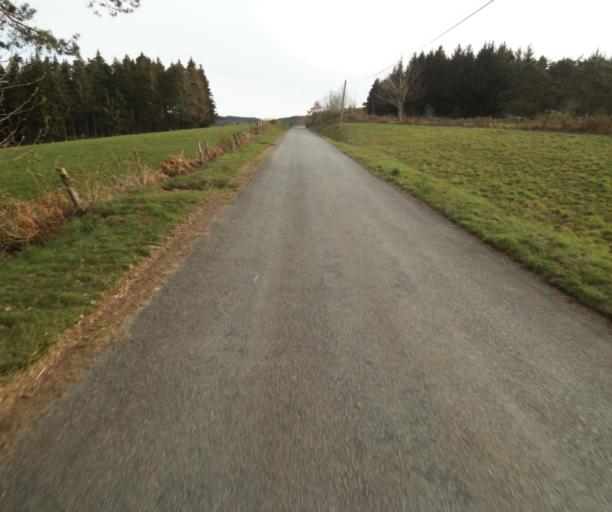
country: FR
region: Limousin
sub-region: Departement de la Correze
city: Treignac
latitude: 45.4630
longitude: 1.8158
